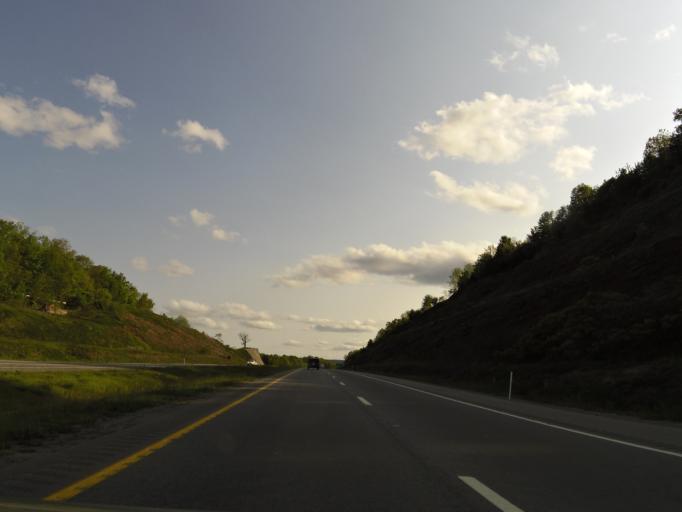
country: US
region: West Virginia
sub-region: Mercer County
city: Princeton
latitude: 37.3337
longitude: -81.1288
